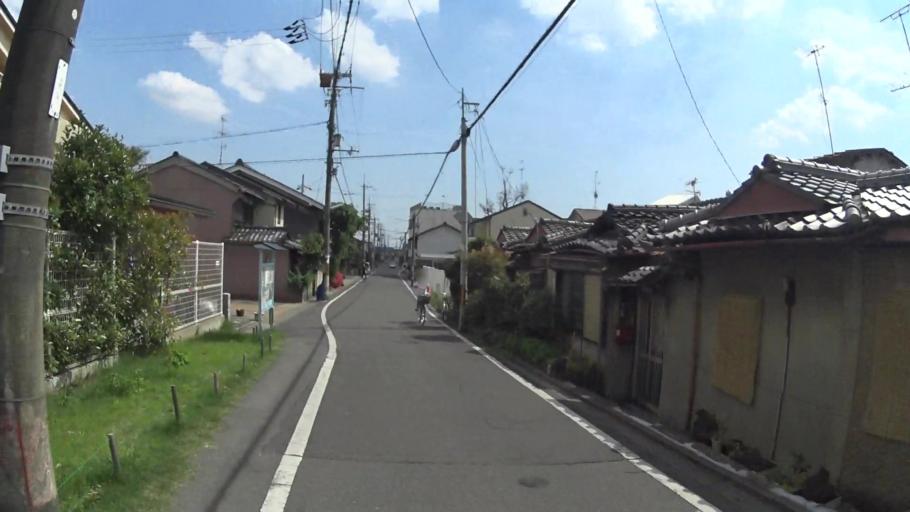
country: JP
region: Kyoto
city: Muko
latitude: 35.0127
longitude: 135.6937
